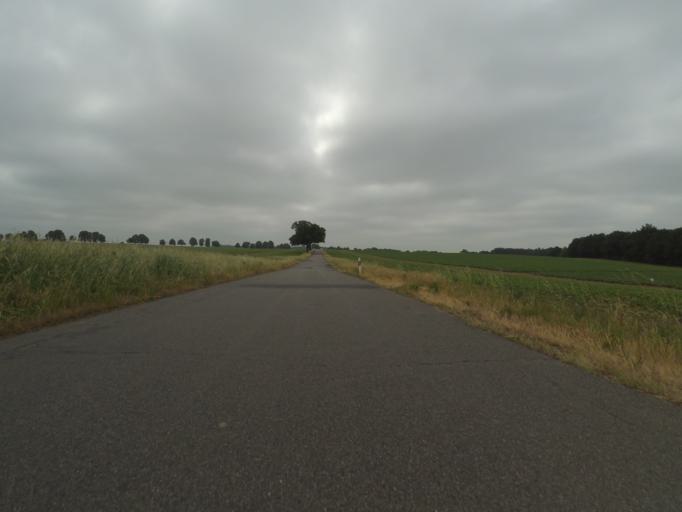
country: DE
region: Mecklenburg-Vorpommern
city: Demen
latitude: 53.6270
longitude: 11.8330
